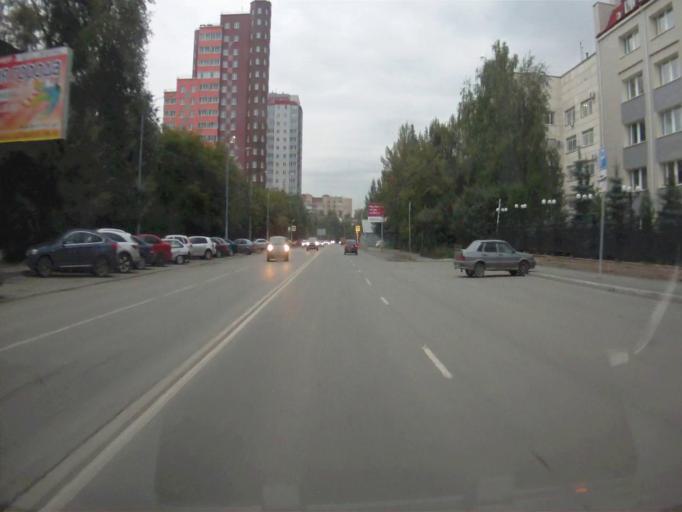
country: RU
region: Chelyabinsk
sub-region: Gorod Chelyabinsk
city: Chelyabinsk
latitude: 55.1502
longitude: 61.3985
